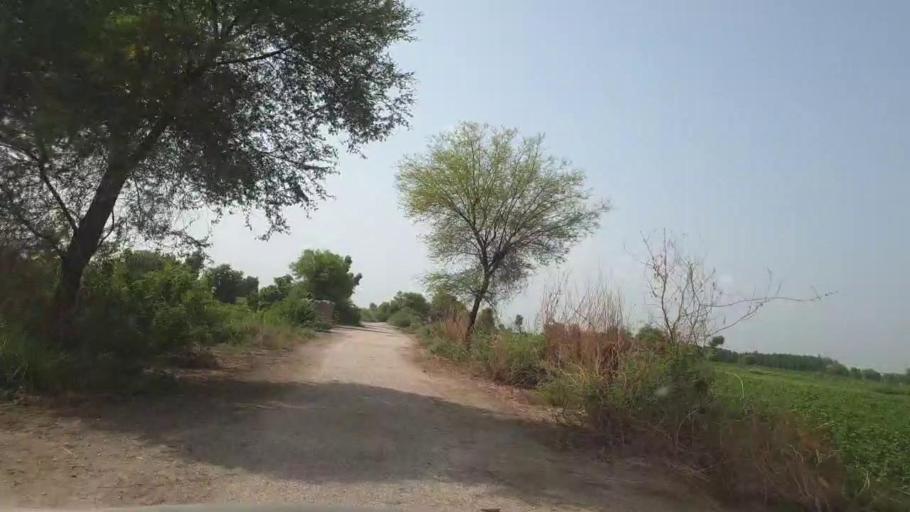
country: PK
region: Sindh
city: Pano Aqil
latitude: 27.7760
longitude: 69.1624
